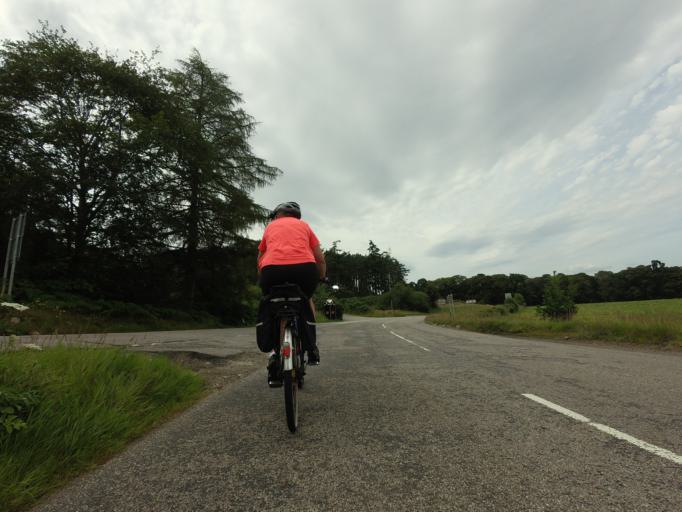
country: GB
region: Scotland
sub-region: Highland
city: Alness
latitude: 57.8535
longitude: -4.3042
